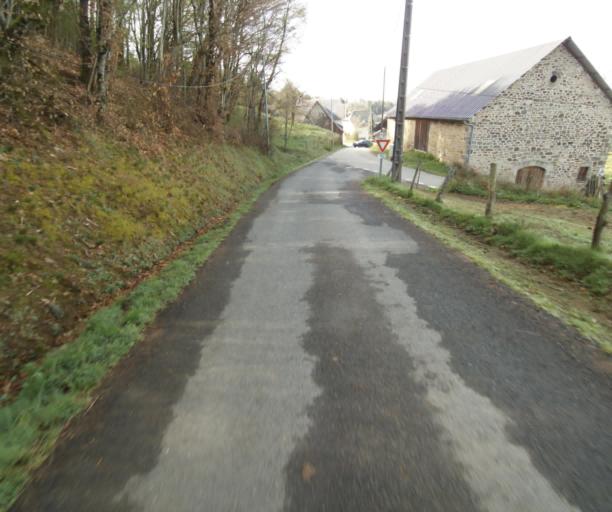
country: FR
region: Limousin
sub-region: Departement de la Correze
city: Laguenne
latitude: 45.2686
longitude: 1.8248
